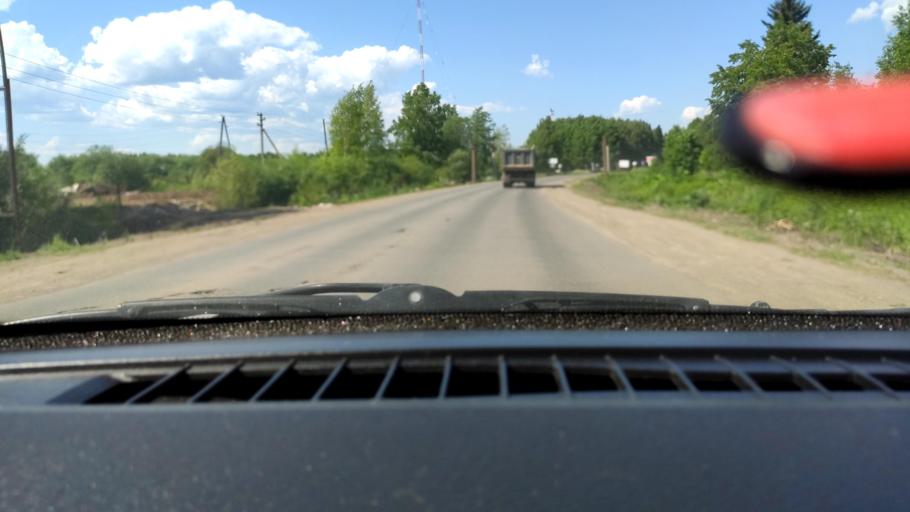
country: RU
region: Perm
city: Sylva
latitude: 58.0202
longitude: 56.7397
